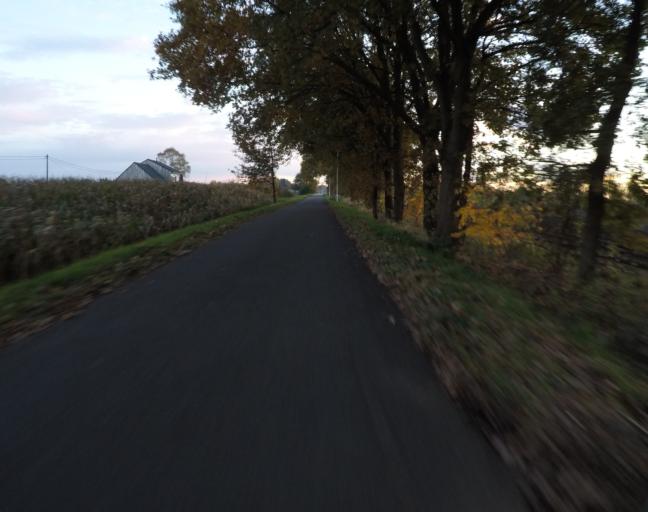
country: BE
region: Flanders
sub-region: Provincie Antwerpen
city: Olen
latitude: 51.1353
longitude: 4.8235
